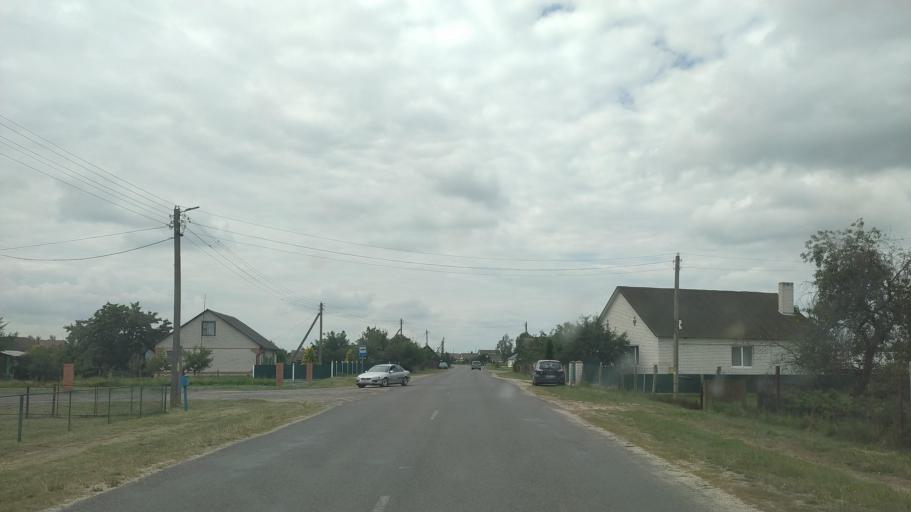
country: BY
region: Brest
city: Byaroza
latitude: 52.5415
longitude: 25.0852
